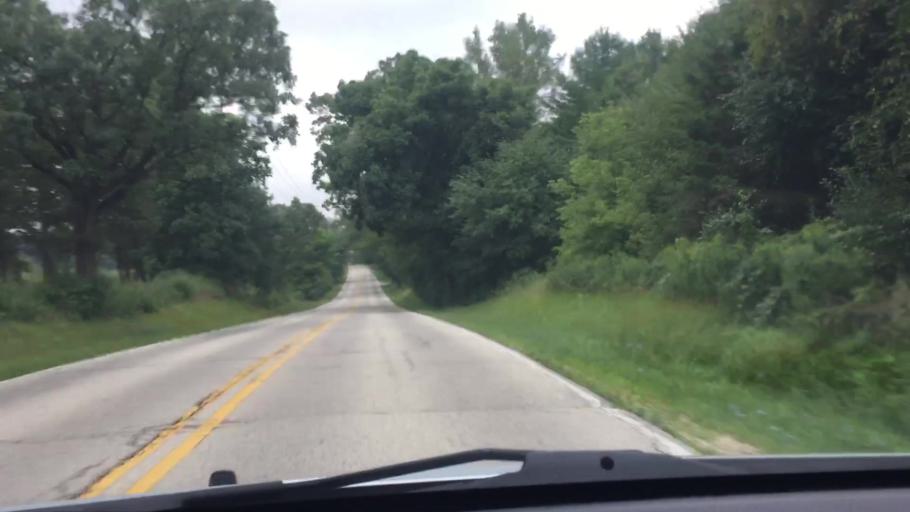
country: US
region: Wisconsin
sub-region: Waukesha County
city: Dousman
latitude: 43.0280
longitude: -88.4428
